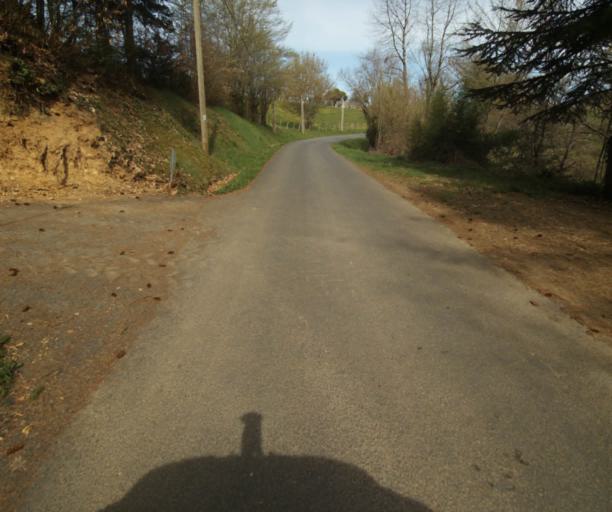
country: FR
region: Limousin
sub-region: Departement de la Correze
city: Correze
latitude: 45.3558
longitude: 1.8154
